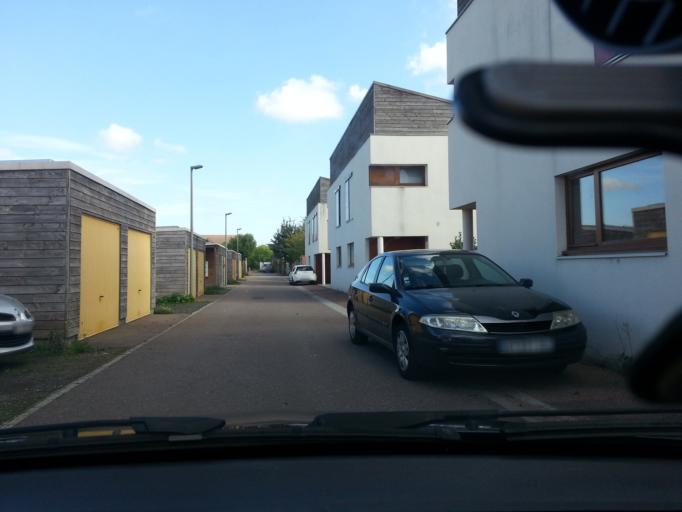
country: FR
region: Bourgogne
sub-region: Departement de Saone-et-Loire
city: Chalon-sur-Saone
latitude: 46.7978
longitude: 4.8524
